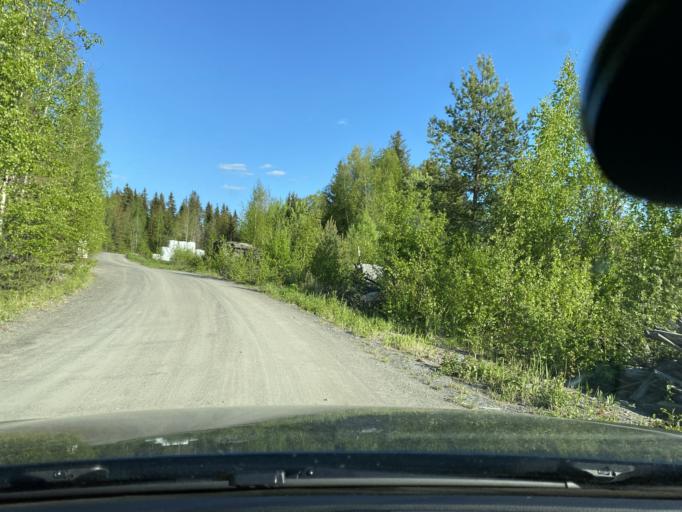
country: FI
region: Pirkanmaa
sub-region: Lounais-Pirkanmaa
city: Punkalaidun
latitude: 61.0754
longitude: 23.0807
